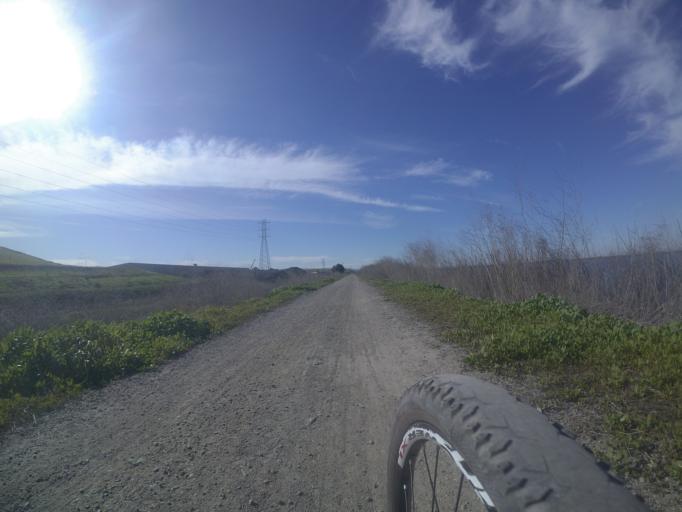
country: US
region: California
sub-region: Santa Clara County
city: Sunnyvale
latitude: 37.4189
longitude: -122.0083
